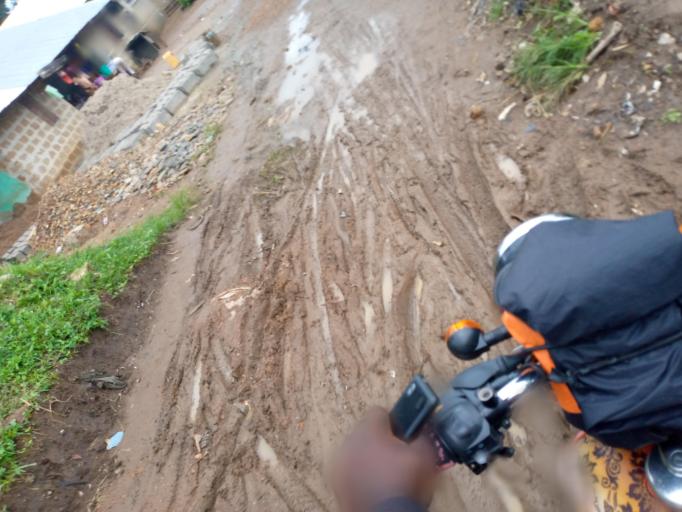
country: SL
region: Eastern Province
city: Kenema
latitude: 7.8709
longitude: -11.1870
